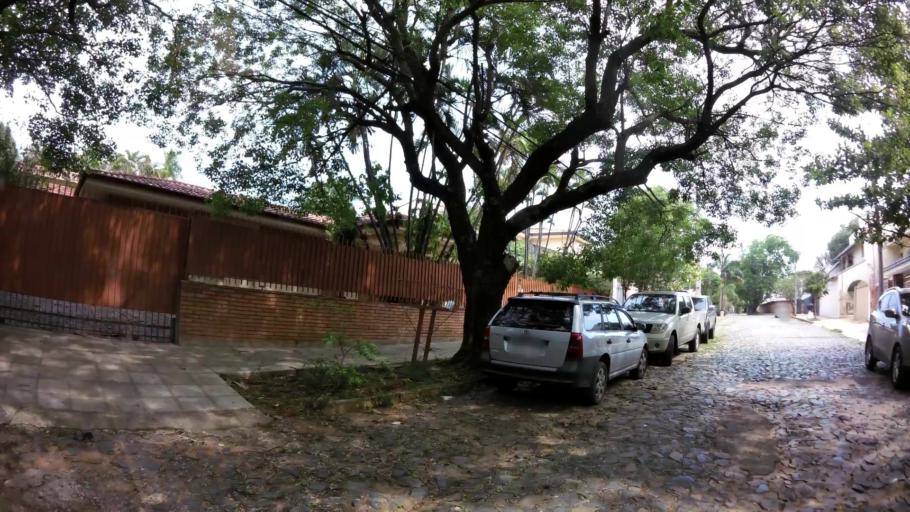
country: PY
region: Asuncion
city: Asuncion
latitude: -25.2773
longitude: -57.5720
